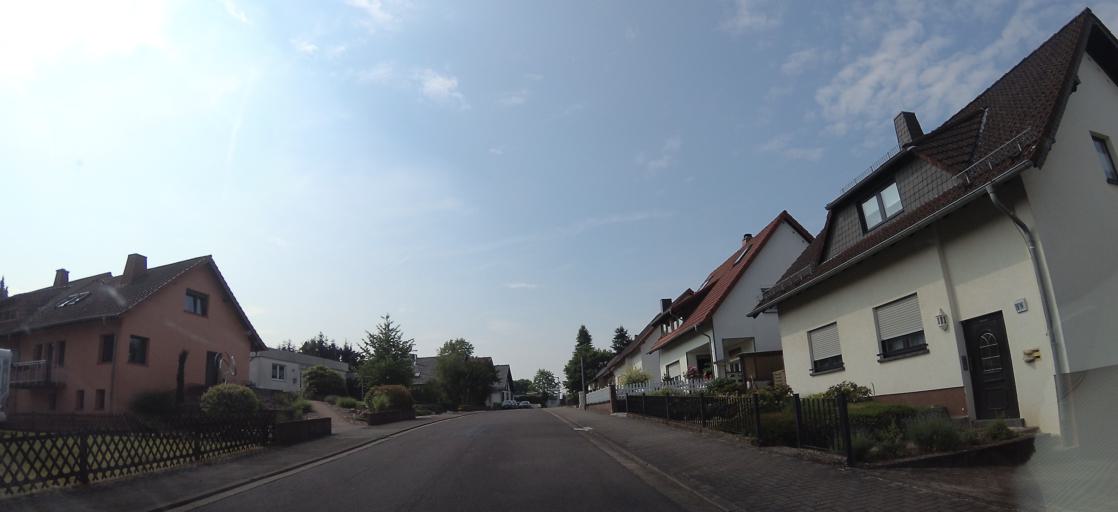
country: DE
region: Saarland
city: Bexbach
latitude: 49.3518
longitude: 7.2730
